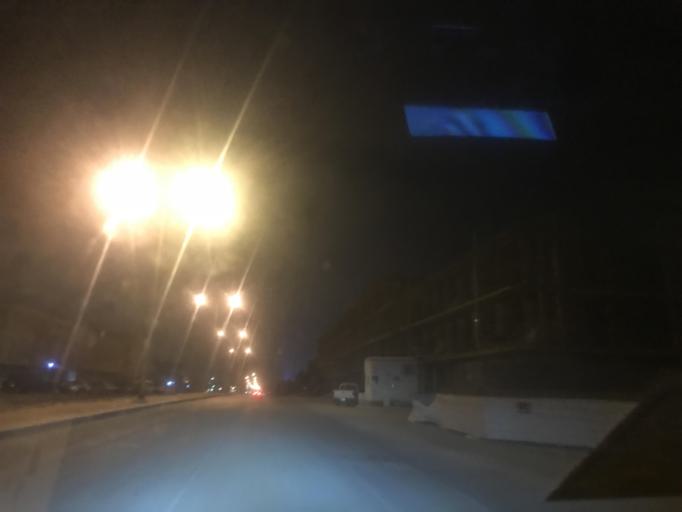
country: SA
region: Ar Riyad
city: Riyadh
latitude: 24.8098
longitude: 46.5887
